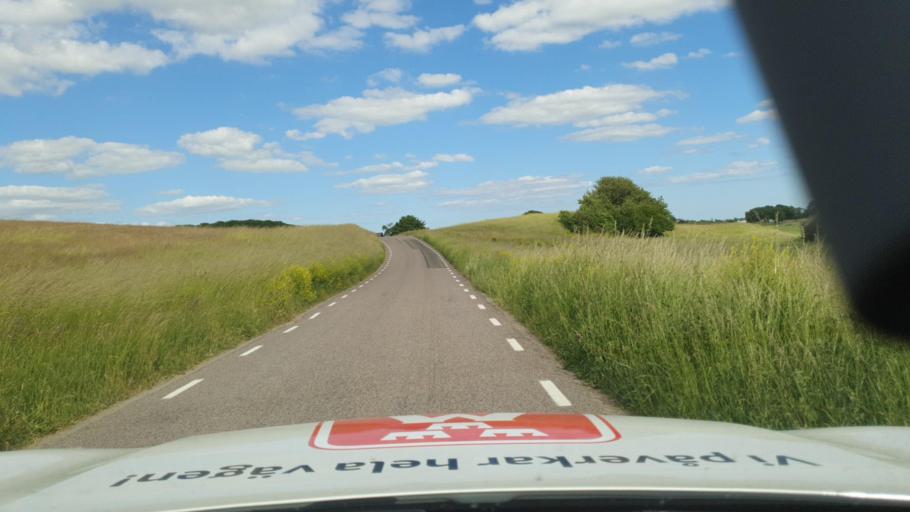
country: SE
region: Skane
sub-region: Ystads Kommun
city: Kopingebro
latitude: 55.4697
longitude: 13.9649
